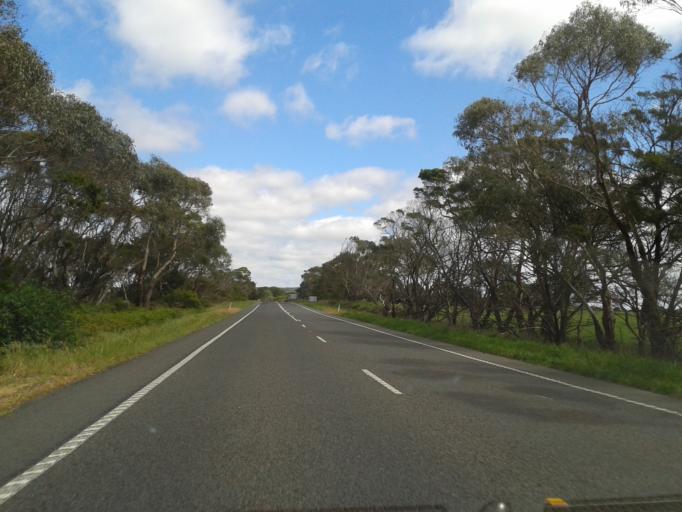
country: AU
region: Victoria
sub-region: Glenelg
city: Portland
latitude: -38.2180
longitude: 141.7915
